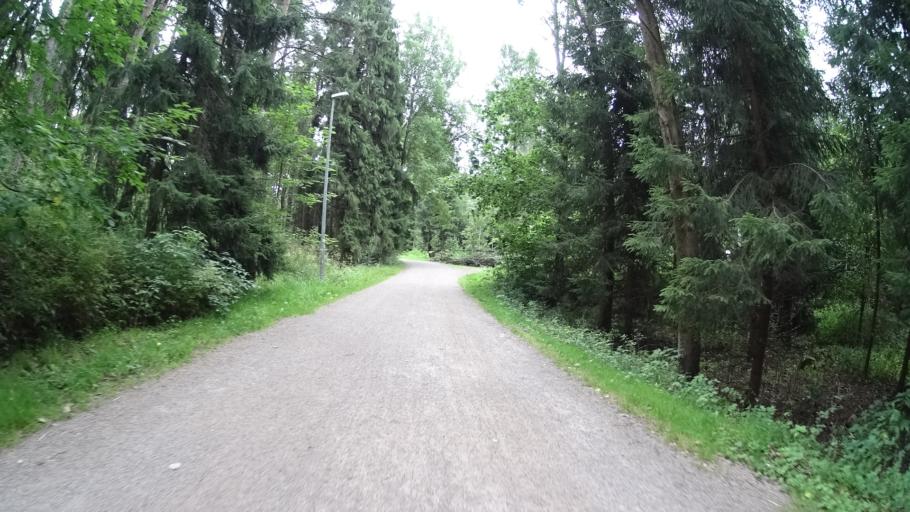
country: FI
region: Uusimaa
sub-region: Helsinki
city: Teekkarikylae
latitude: 60.2046
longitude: 24.8624
